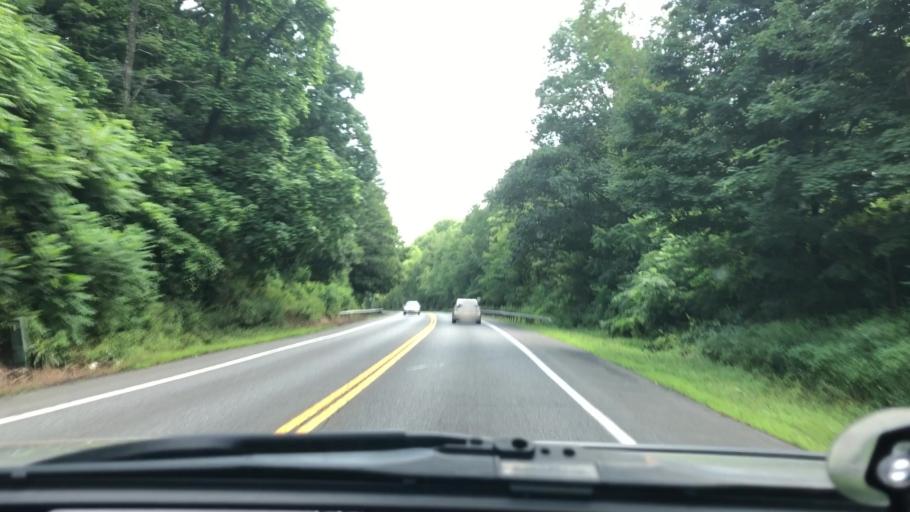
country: US
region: New York
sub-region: Ulster County
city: Saugerties
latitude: 42.1188
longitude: -73.9876
